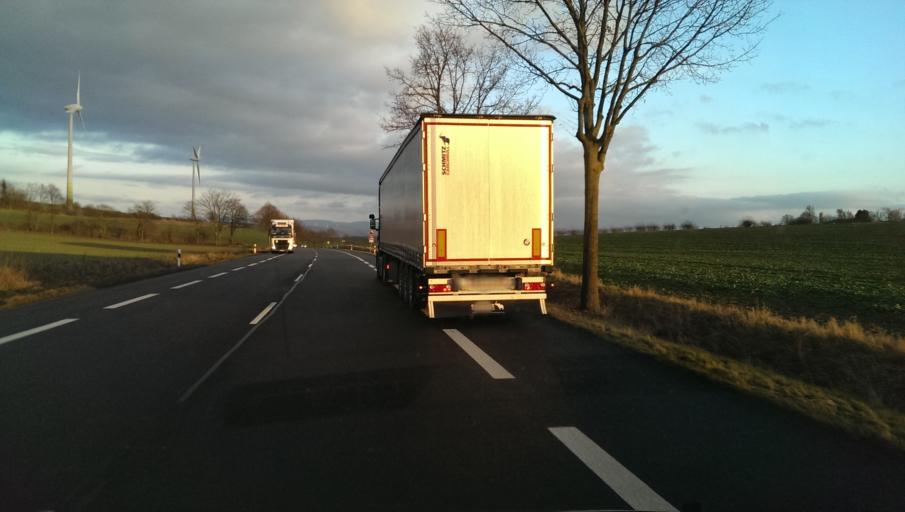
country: DE
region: Lower Saxony
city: Einbeck
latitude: 51.8651
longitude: 9.8981
